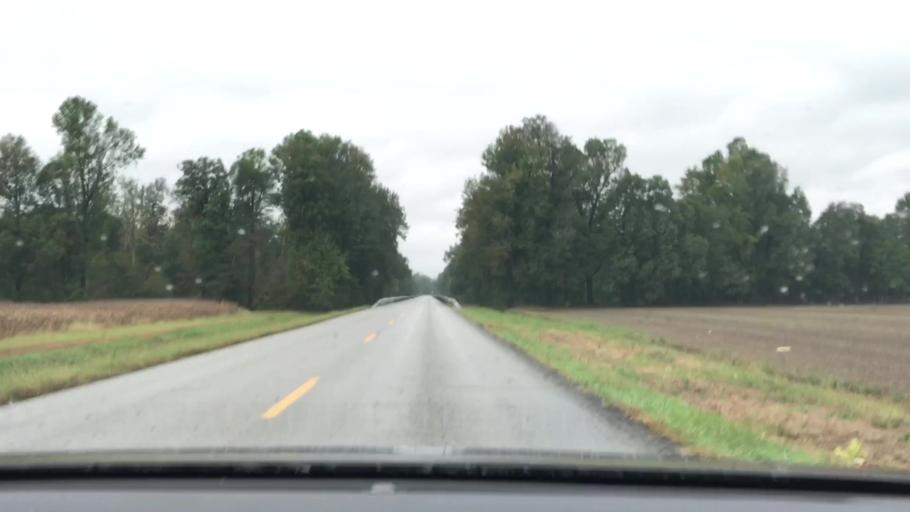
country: US
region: Kentucky
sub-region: McLean County
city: Calhoun
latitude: 37.3963
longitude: -87.2905
